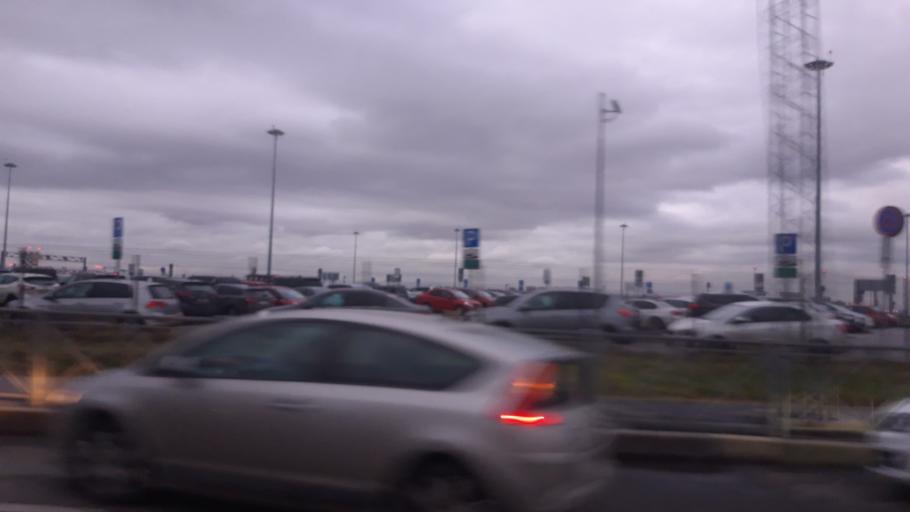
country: RU
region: St.-Petersburg
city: Dachnoye
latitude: 59.7969
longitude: 30.2816
